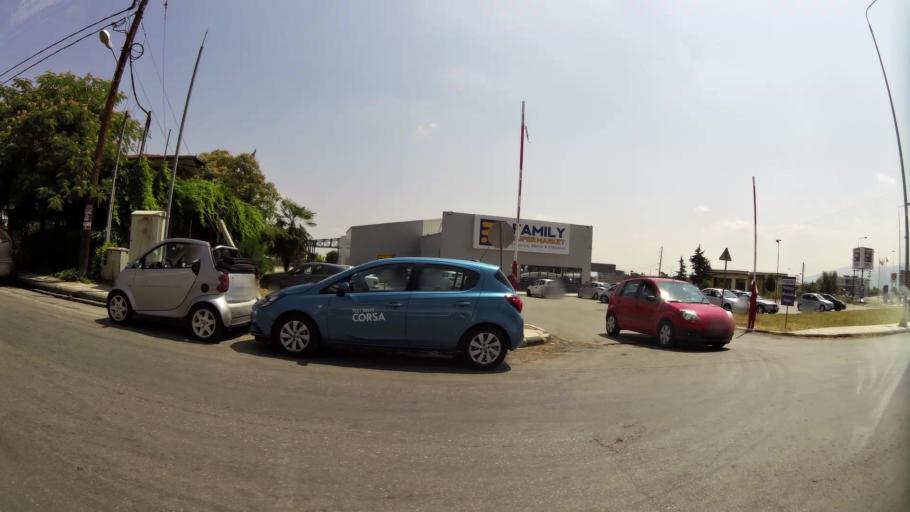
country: GR
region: Central Macedonia
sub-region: Nomos Imathias
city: Veroia
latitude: 40.5287
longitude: 22.2086
